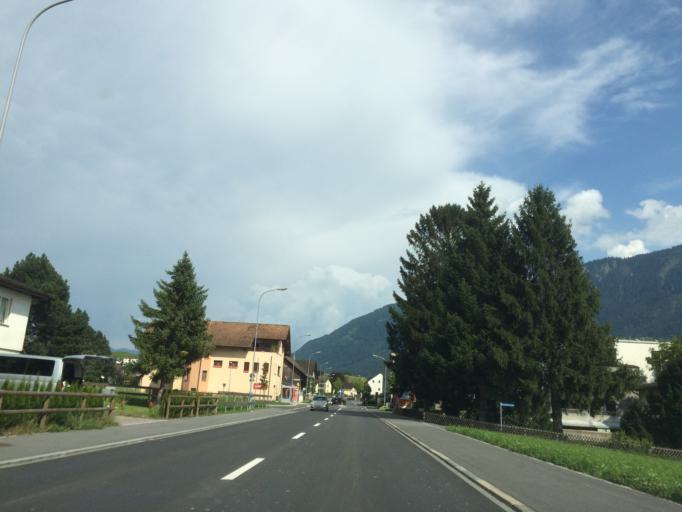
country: LI
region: Eschen
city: Eschen
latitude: 47.2094
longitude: 9.5180
